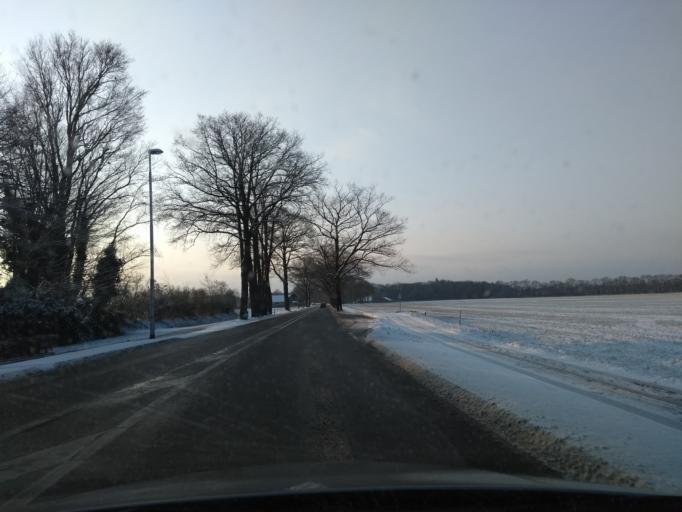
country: NL
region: Overijssel
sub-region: Gemeente Almelo
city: Almelo
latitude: 52.3032
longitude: 6.6558
